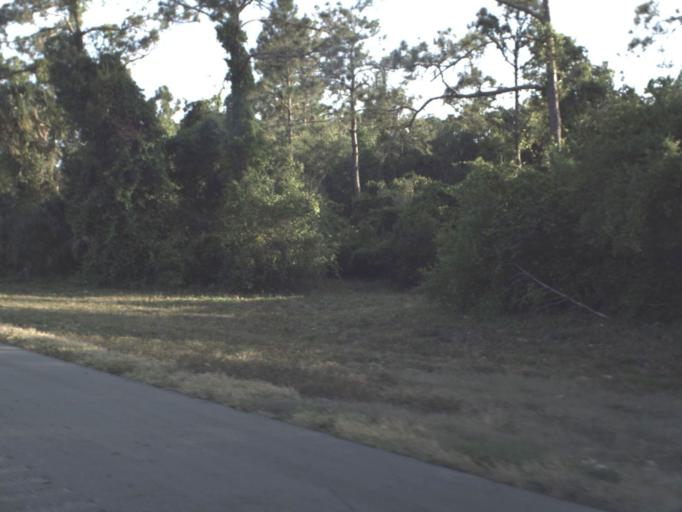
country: US
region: Florida
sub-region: Brevard County
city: Mims
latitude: 28.6891
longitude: -80.8793
